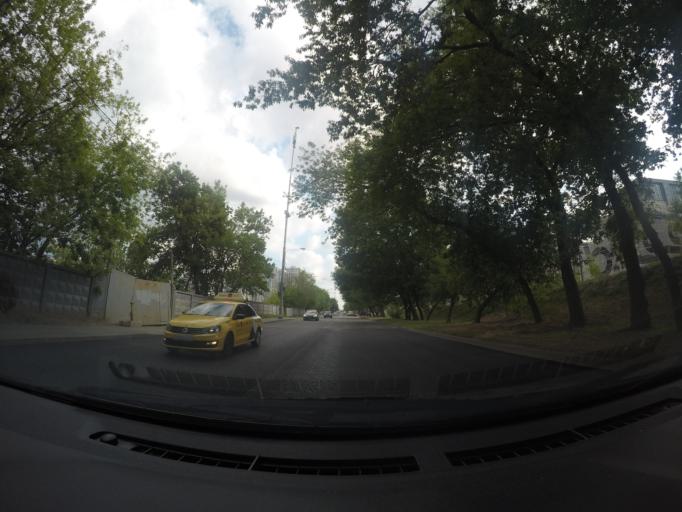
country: RU
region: Moscow
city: Sviblovo
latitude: 55.8518
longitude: 37.6261
